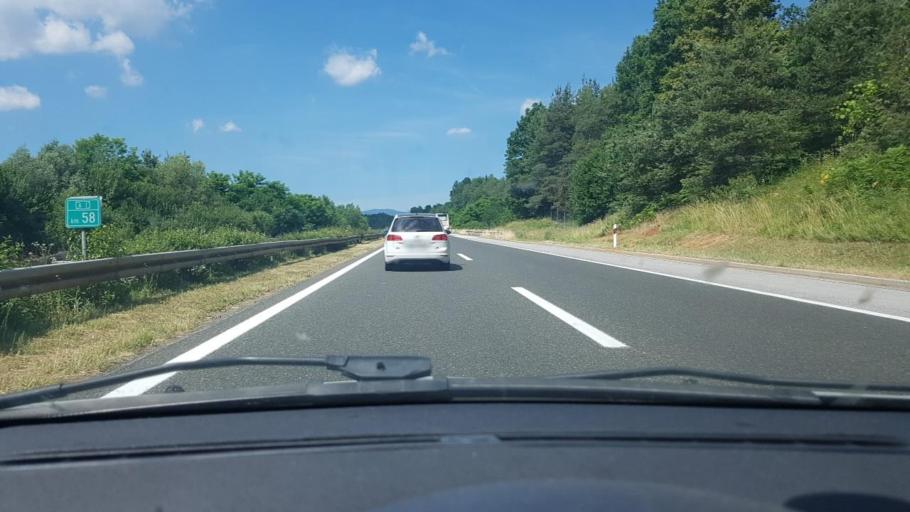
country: HR
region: Karlovacka
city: Ozalj
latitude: 45.4438
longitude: 15.3520
